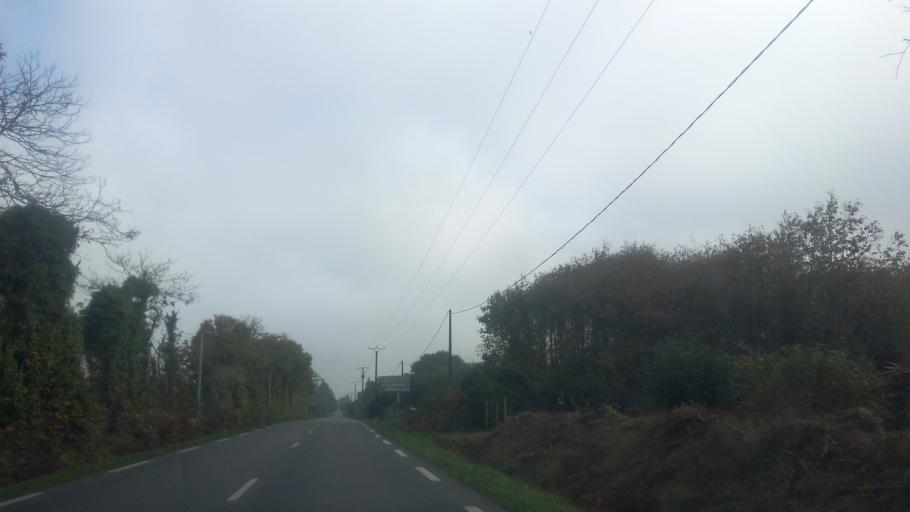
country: FR
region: Pays de la Loire
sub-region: Departement de la Loire-Atlantique
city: Avessac
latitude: 47.6366
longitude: -1.9638
